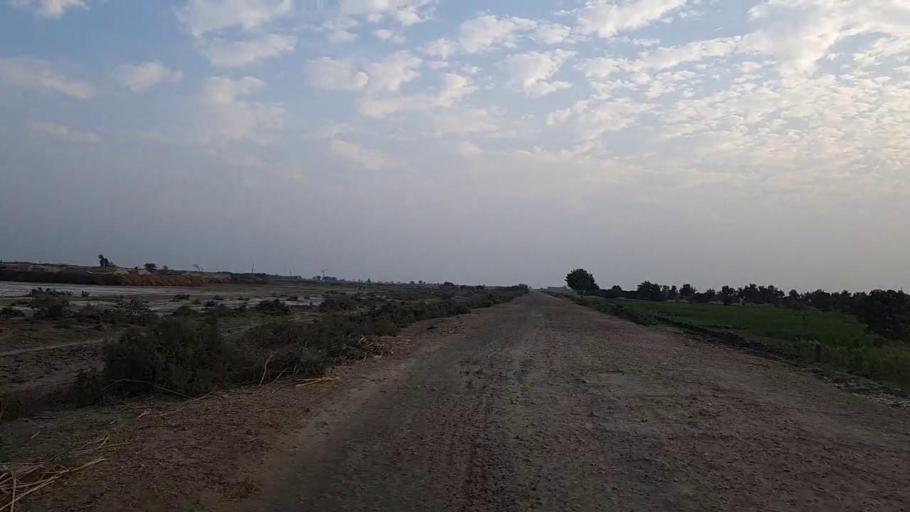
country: PK
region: Sindh
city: Pithoro
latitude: 25.4663
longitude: 69.3466
